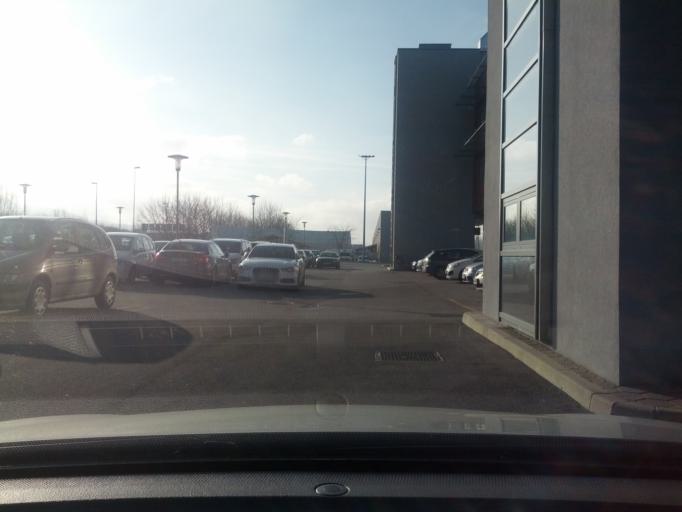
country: SI
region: Skofljica
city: Lavrica
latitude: 46.0209
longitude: 14.5402
